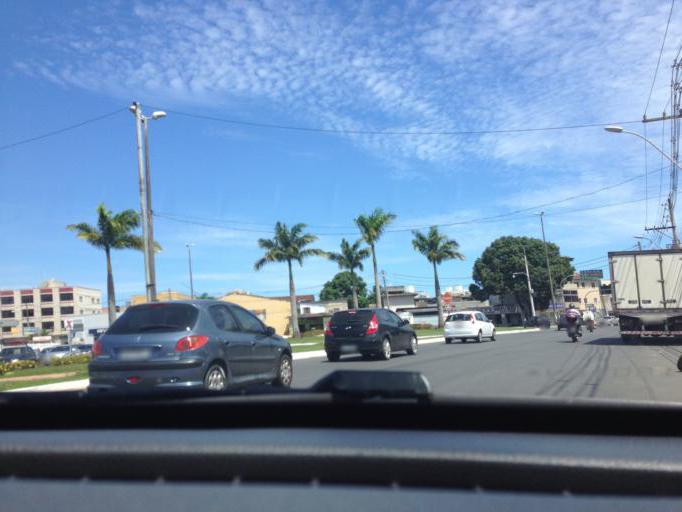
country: BR
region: Espirito Santo
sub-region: Guarapari
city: Guarapari
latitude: -20.6532
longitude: -40.4977
